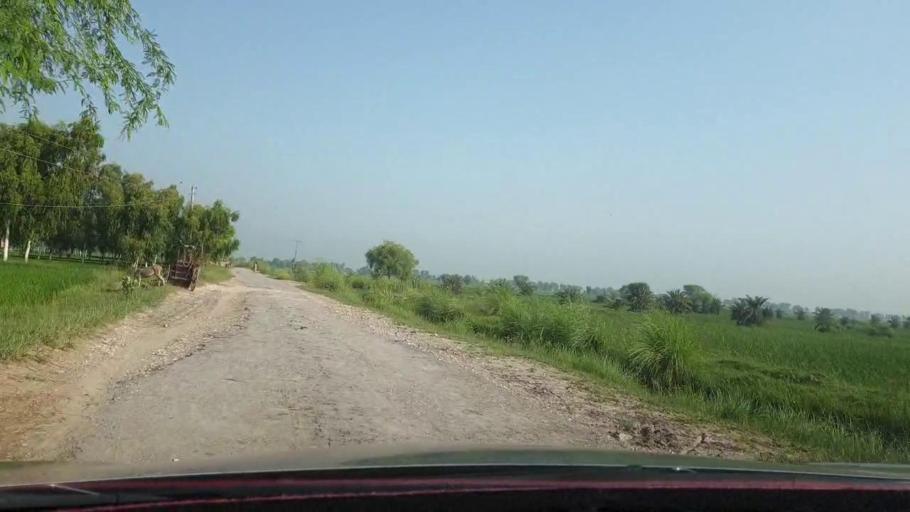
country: PK
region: Sindh
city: Nasirabad
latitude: 27.4411
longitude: 67.9206
